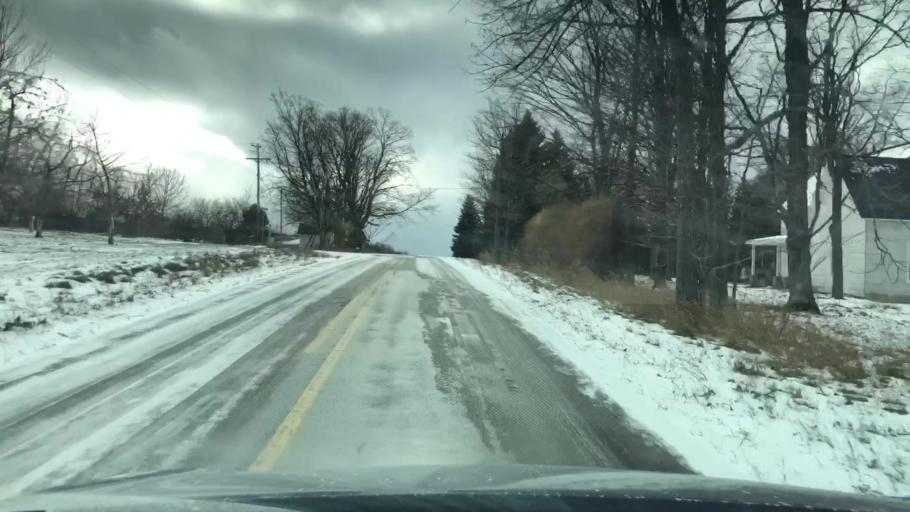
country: US
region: Michigan
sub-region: Antrim County
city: Elk Rapids
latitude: 44.9362
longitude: -85.5155
